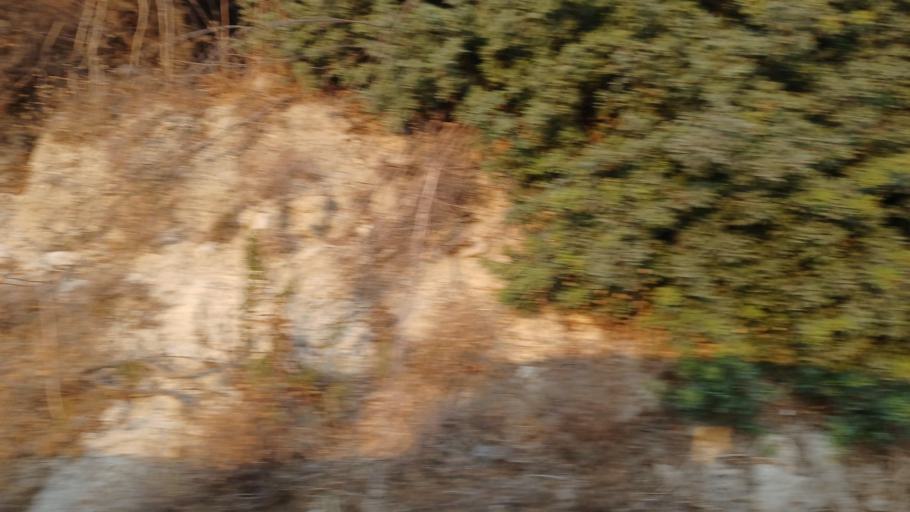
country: CY
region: Limassol
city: Pissouri
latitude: 34.6828
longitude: 32.6939
